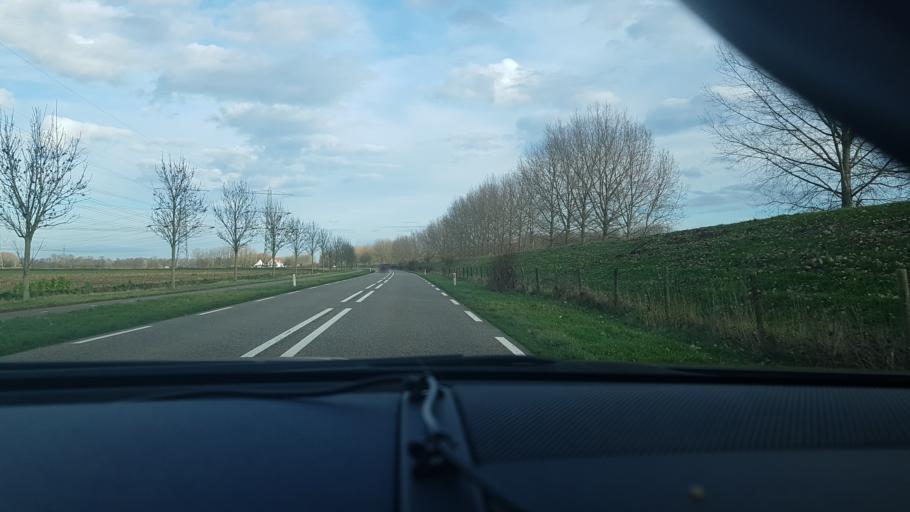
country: NL
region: Limburg
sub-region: Gemeente Leudal
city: Haelen
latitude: 51.2079
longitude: 5.9618
